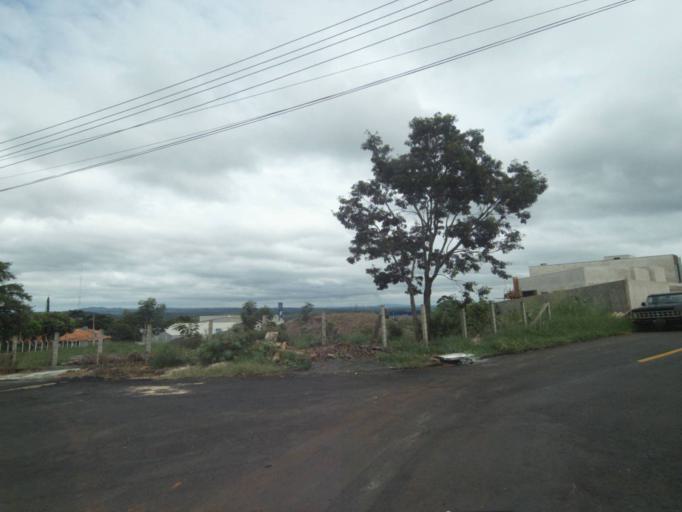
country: BR
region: Parana
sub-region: Telemaco Borba
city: Telemaco Borba
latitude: -24.3331
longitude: -50.6473
